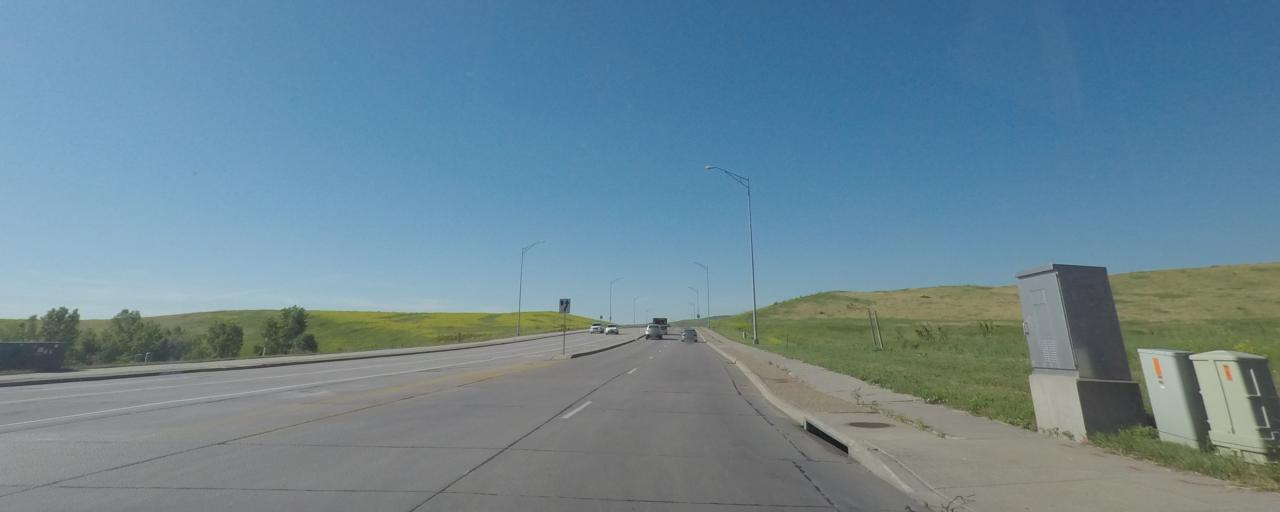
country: US
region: South Dakota
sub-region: Pennington County
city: Rapid City
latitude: 44.0429
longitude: -103.2192
